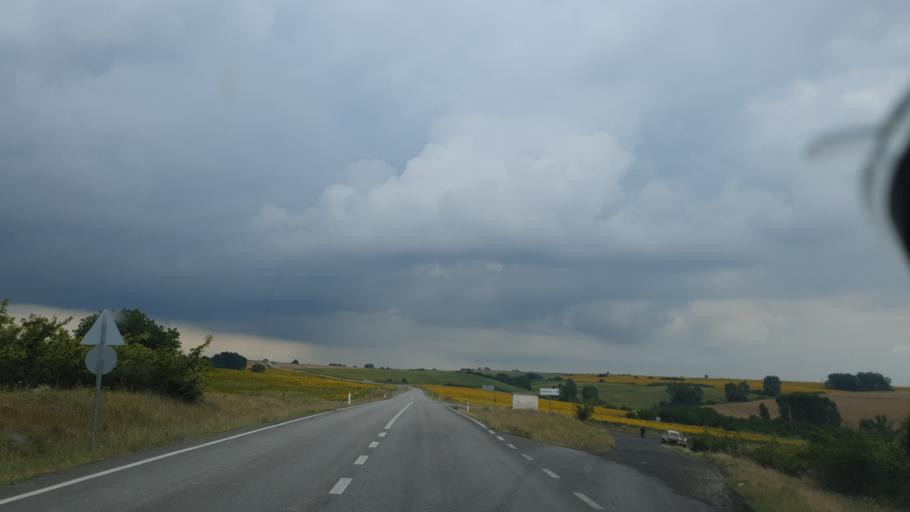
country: TR
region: Tekirdag
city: Hayrabolu
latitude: 41.2212
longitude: 27.0066
